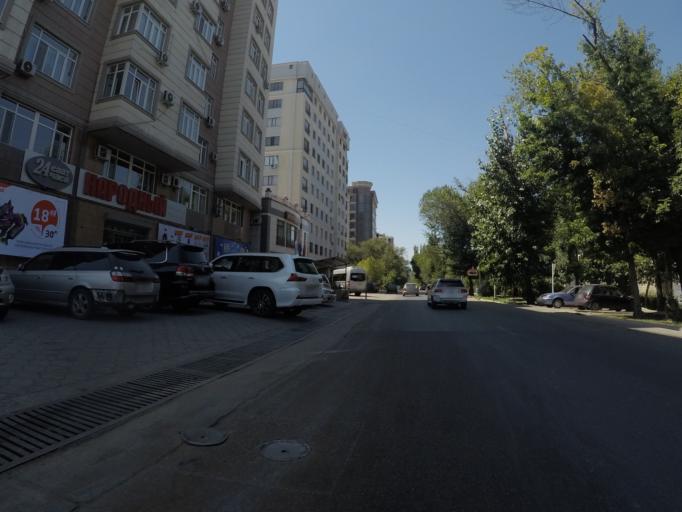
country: KG
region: Chuy
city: Bishkek
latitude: 42.8679
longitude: 74.5821
